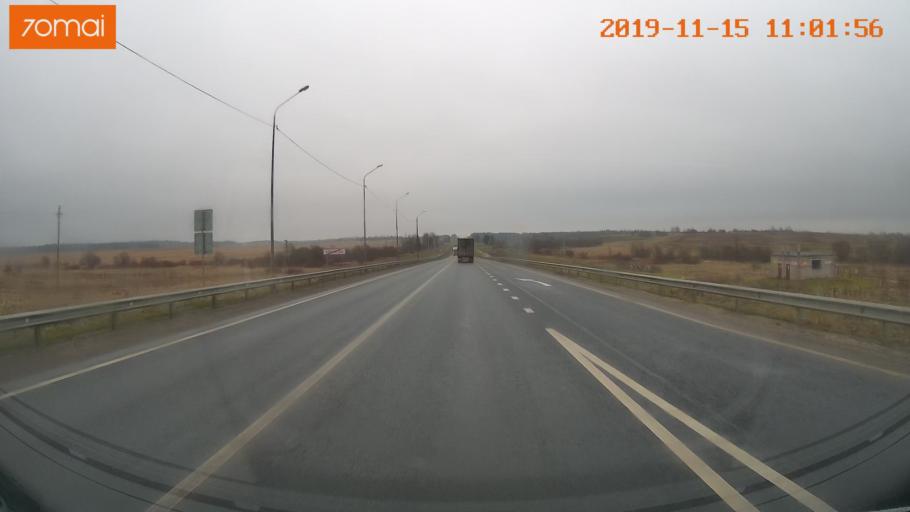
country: RU
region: Vologda
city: Chebsara
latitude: 59.1309
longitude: 38.9304
